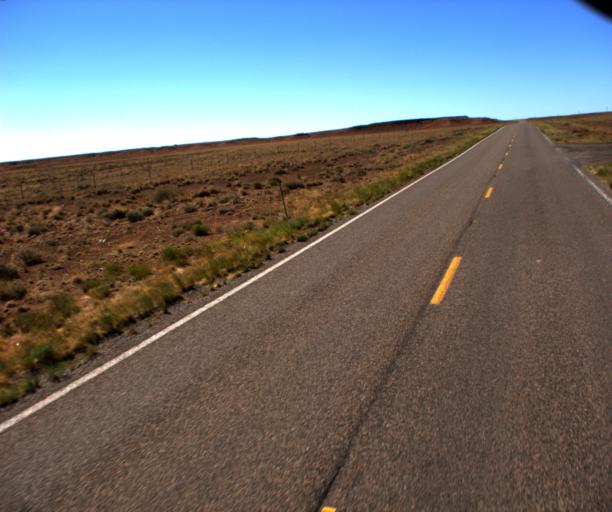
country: US
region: Arizona
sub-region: Coconino County
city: LeChee
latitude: 35.2088
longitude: -110.9492
